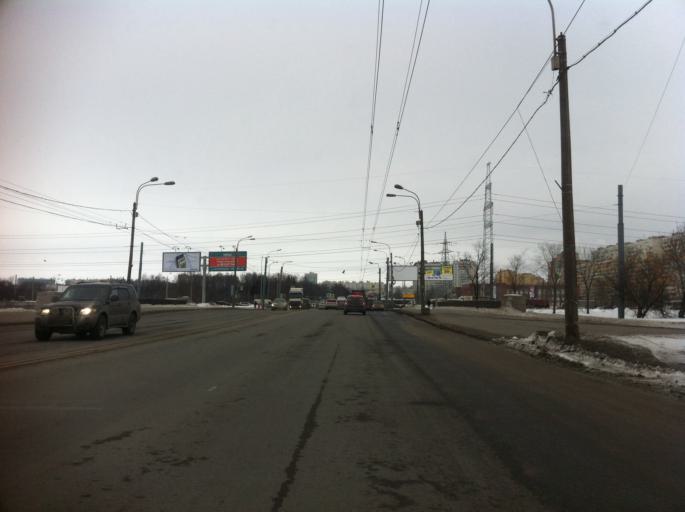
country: RU
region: St.-Petersburg
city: Uritsk
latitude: 59.8447
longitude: 30.1755
